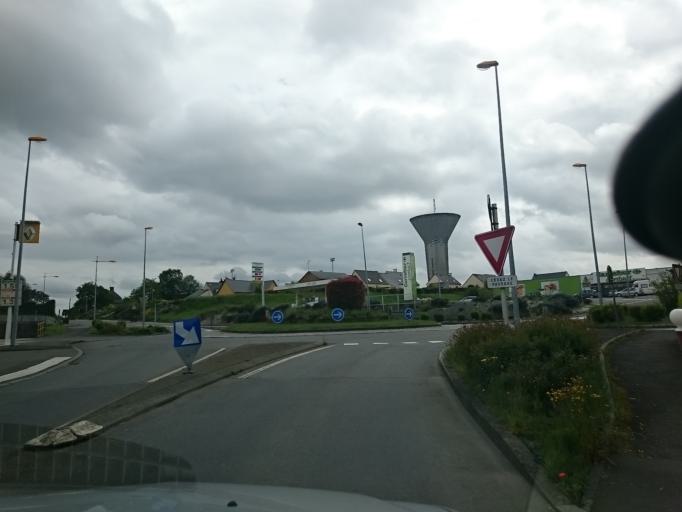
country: FR
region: Brittany
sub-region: Departement d'Ille-et-Vilaine
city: Antrain
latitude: 48.4582
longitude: -1.4817
